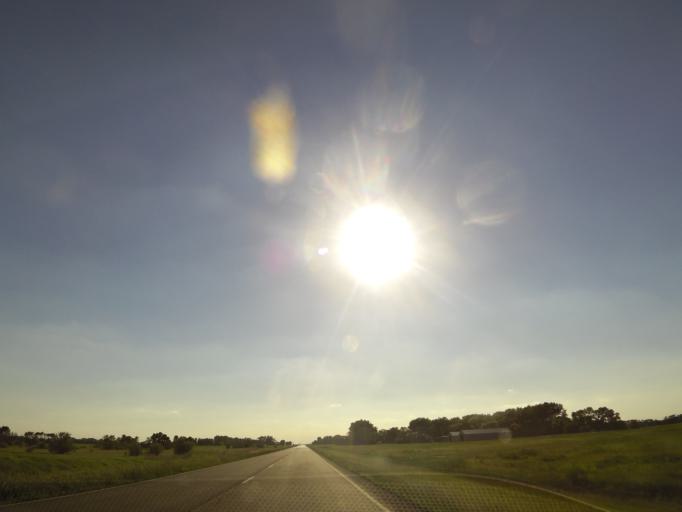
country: US
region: North Dakota
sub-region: Grand Forks County
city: Grand Forks Air Force Base
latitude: 48.1361
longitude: -97.1969
